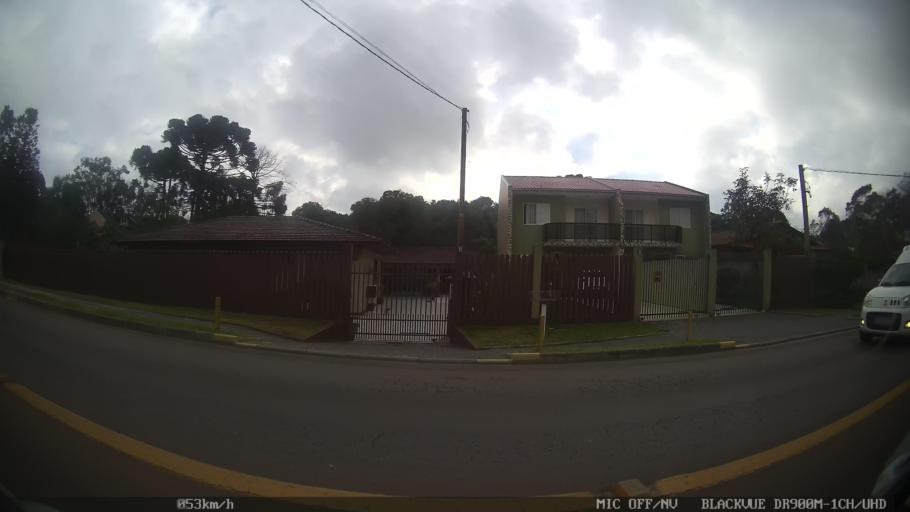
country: BR
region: Parana
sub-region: Curitiba
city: Curitiba
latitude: -25.3716
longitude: -49.2303
